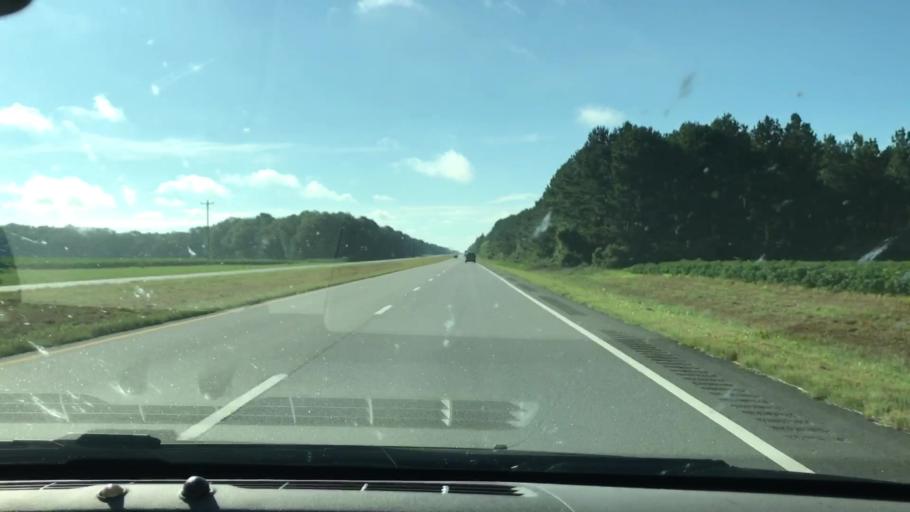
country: US
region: Georgia
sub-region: Terrell County
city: Dawson
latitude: 31.6963
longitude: -84.3191
